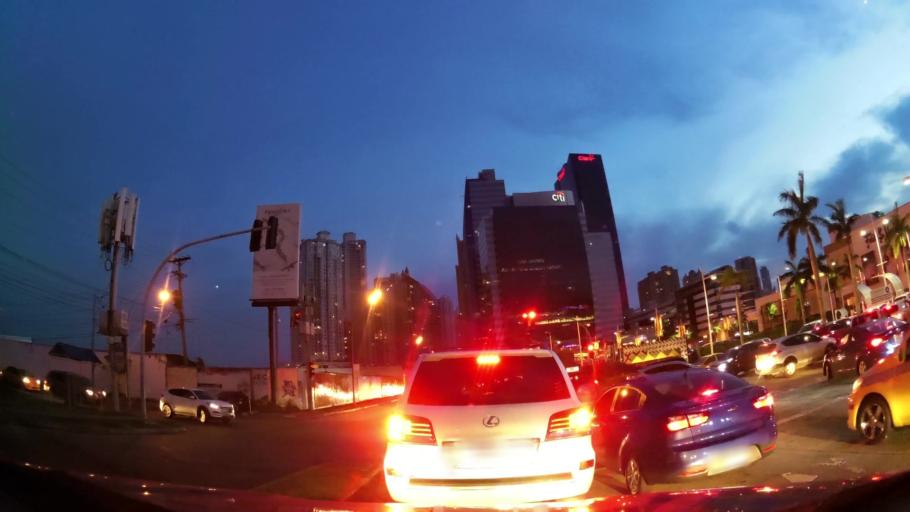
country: PA
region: Panama
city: Panama
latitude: 8.9849
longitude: -79.5092
